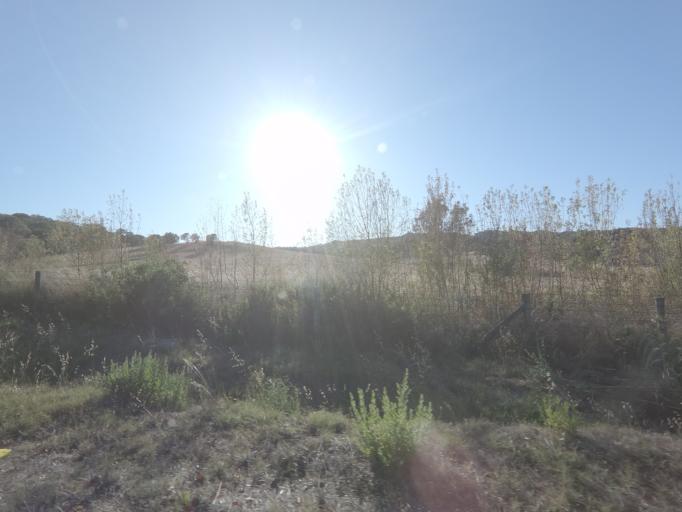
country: PT
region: Setubal
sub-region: Palmela
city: Quinta do Anjo
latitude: 38.5148
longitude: -8.9708
